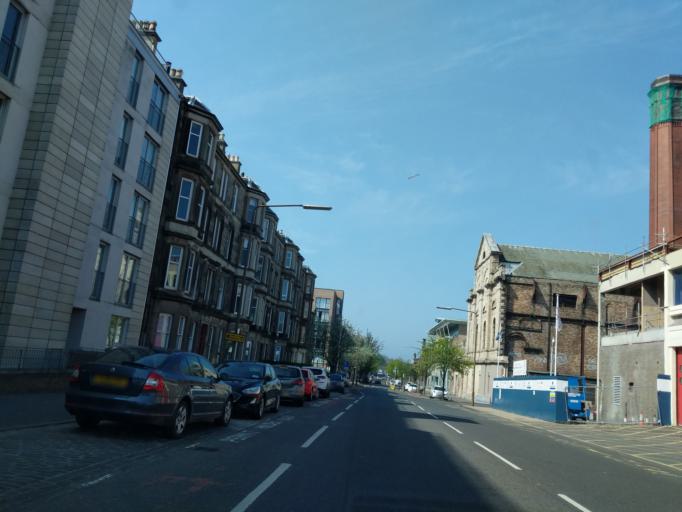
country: GB
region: Scotland
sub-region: Edinburgh
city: Edinburgh
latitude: 55.9635
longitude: -3.1846
